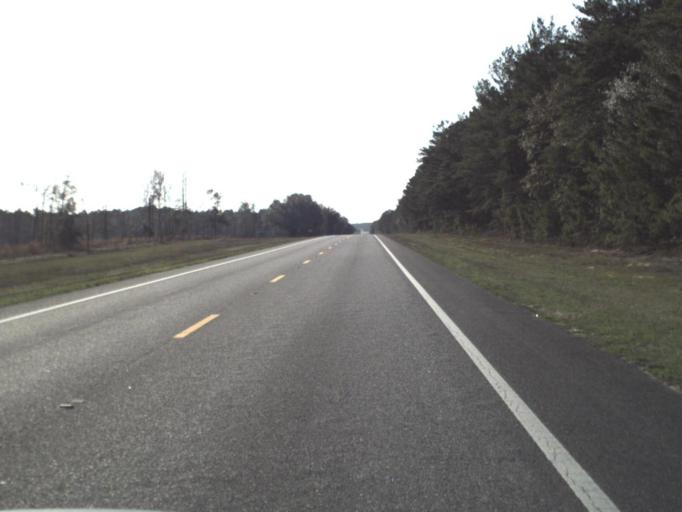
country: US
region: Florida
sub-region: Bay County
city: Youngstown
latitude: 30.4277
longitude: -85.5791
